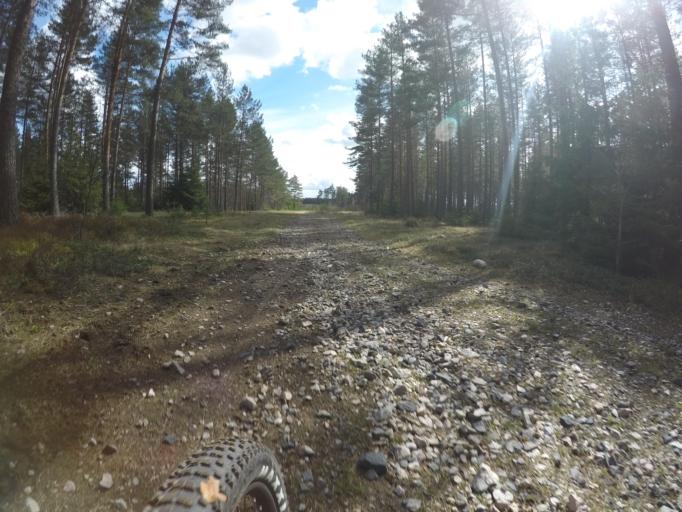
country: SE
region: Vaestmanland
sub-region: Kungsors Kommun
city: Kungsoer
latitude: 59.3494
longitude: 16.1070
